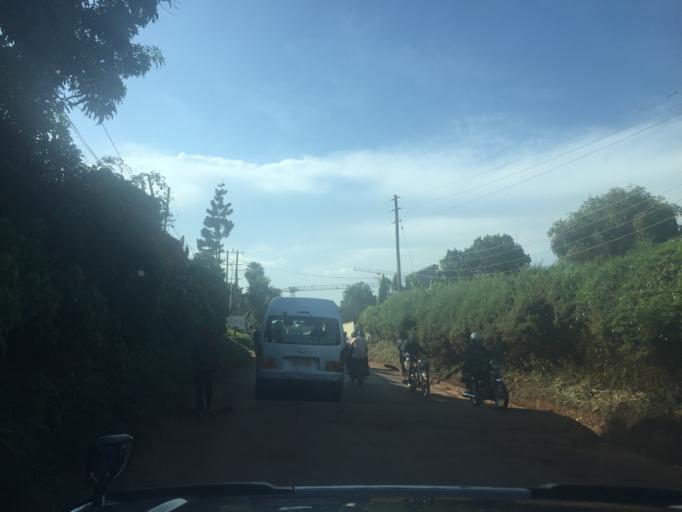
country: UG
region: Central Region
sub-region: Kampala District
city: Kampala
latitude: 0.2988
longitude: 32.5928
